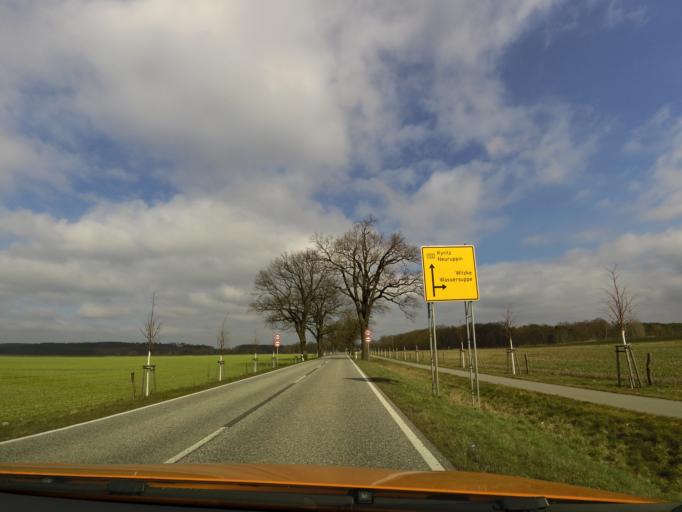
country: DE
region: Brandenburg
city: Rhinow
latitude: 52.6788
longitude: 12.3536
